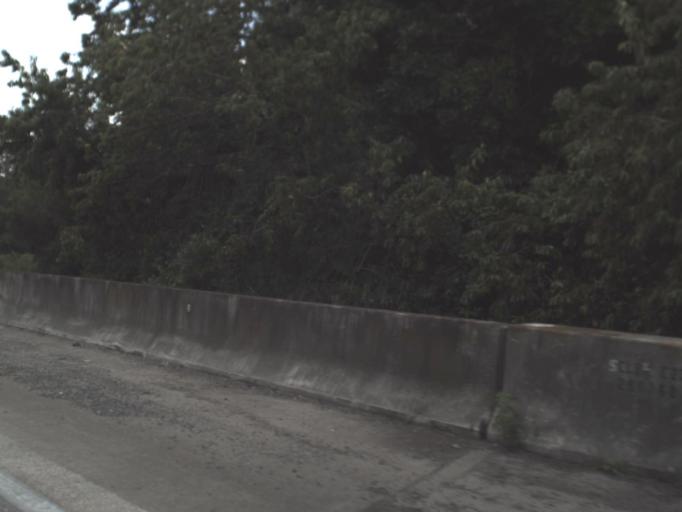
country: US
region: Florida
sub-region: Alachua County
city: Alachua
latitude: 29.7754
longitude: -82.5095
